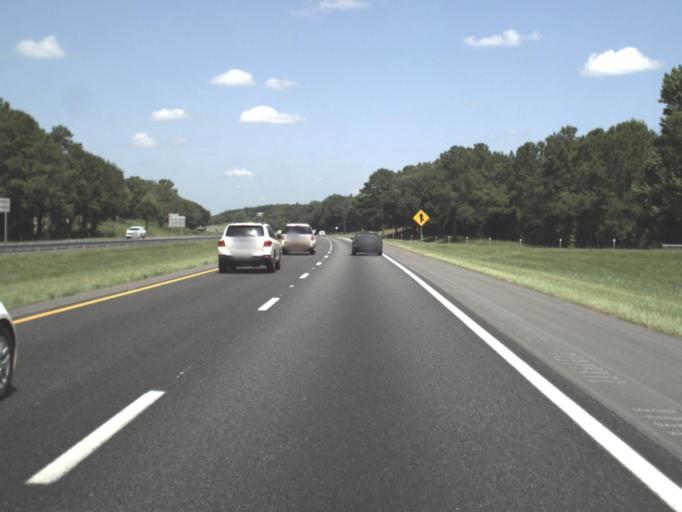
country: US
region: Florida
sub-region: Madison County
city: Madison
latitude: 30.4324
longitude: -83.4581
